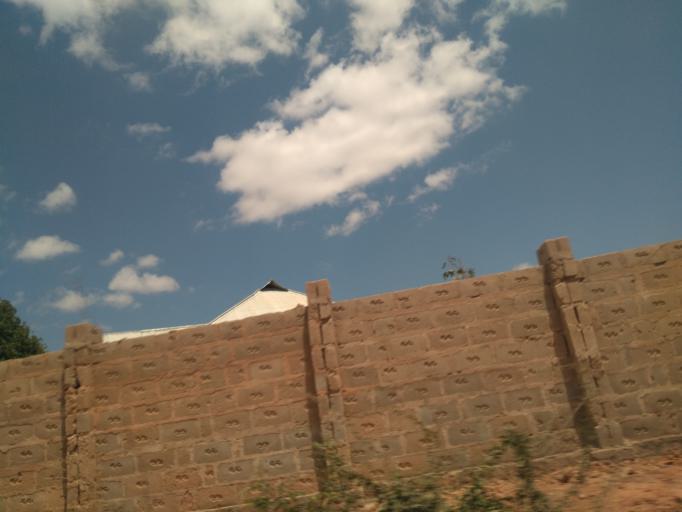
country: TZ
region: Dodoma
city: Kisasa
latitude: -6.1673
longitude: 35.7798
